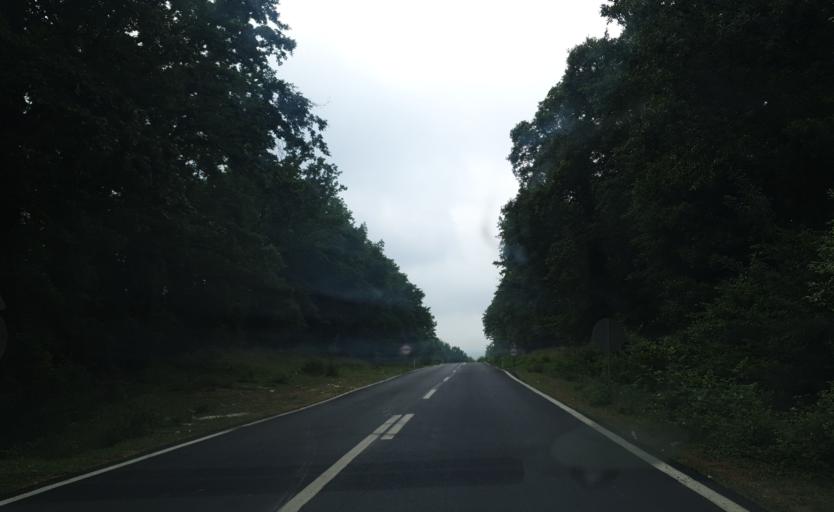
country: TR
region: Kirklareli
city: Salmydessus
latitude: 41.6024
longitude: 28.0871
